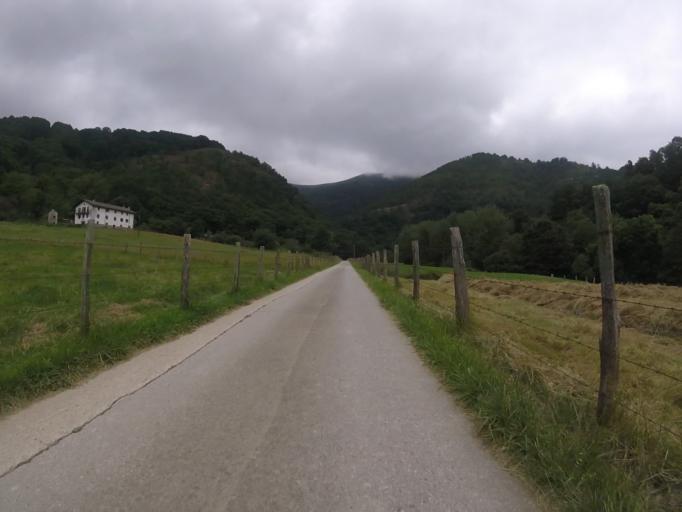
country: ES
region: Navarre
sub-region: Provincia de Navarra
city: Sunbilla
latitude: 43.1863
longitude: -1.6713
